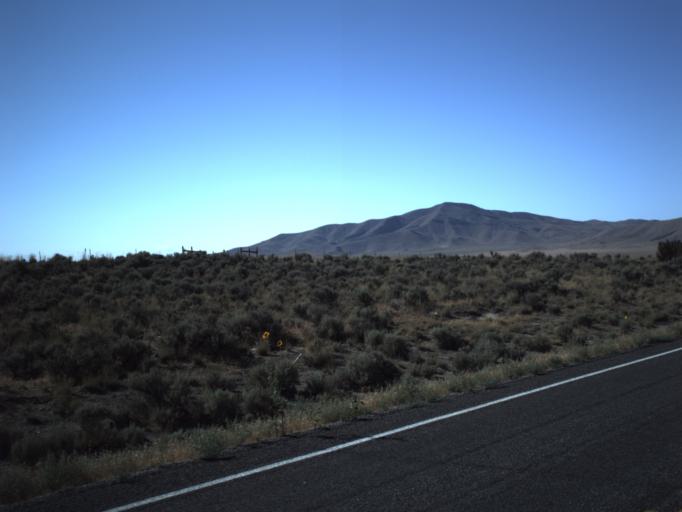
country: US
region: Utah
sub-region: Juab County
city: Mona
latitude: 39.7246
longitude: -112.1969
